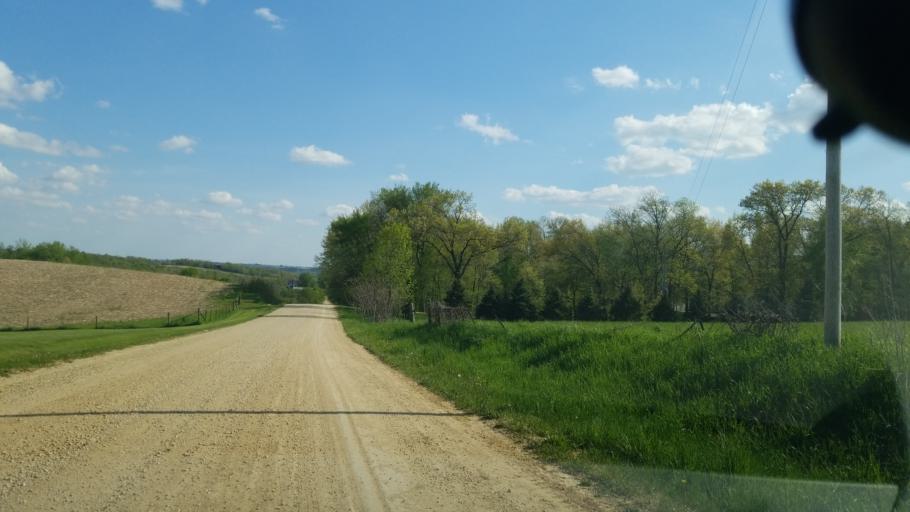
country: US
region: Iowa
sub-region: Jackson County
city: Maquoketa
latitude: 42.2002
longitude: -90.7294
